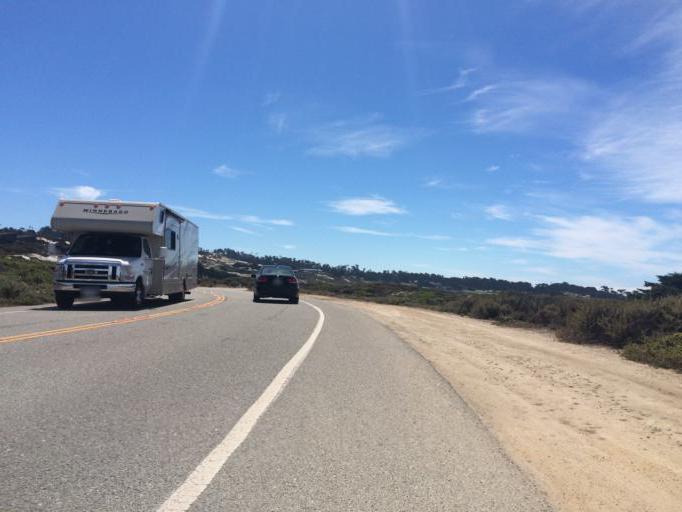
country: US
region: California
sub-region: Monterey County
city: Del Monte Forest
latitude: 36.5917
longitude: -121.9630
